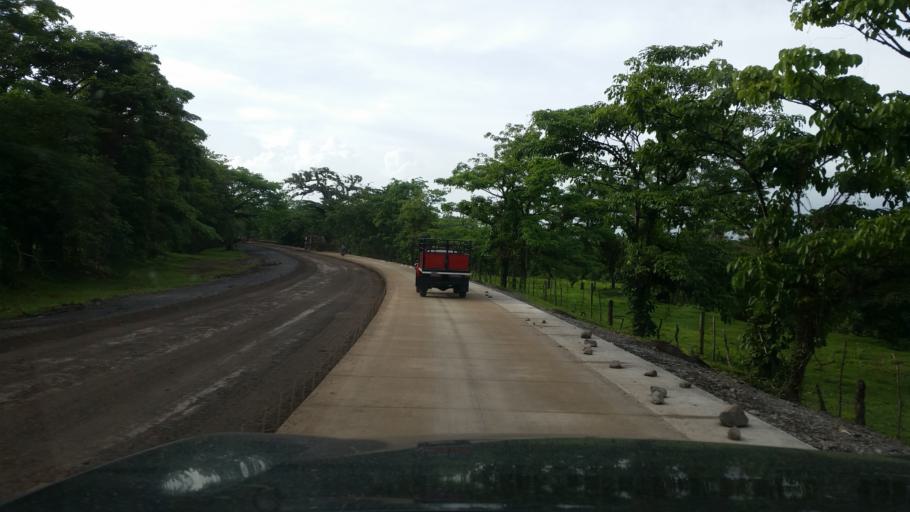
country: NI
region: Matagalpa
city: Rio Blanco
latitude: 13.0789
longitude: -85.0599
